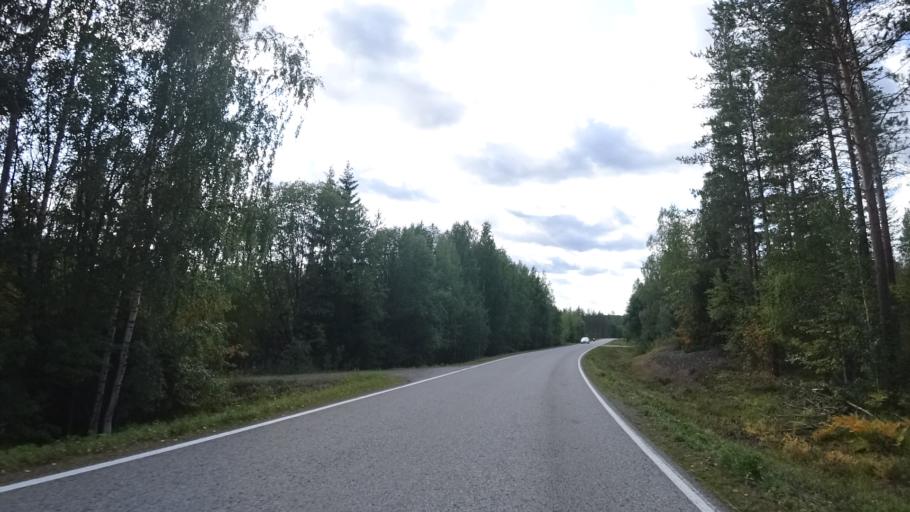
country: RU
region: Republic of Karelia
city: Vyartsilya
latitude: 62.2223
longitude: 30.6471
